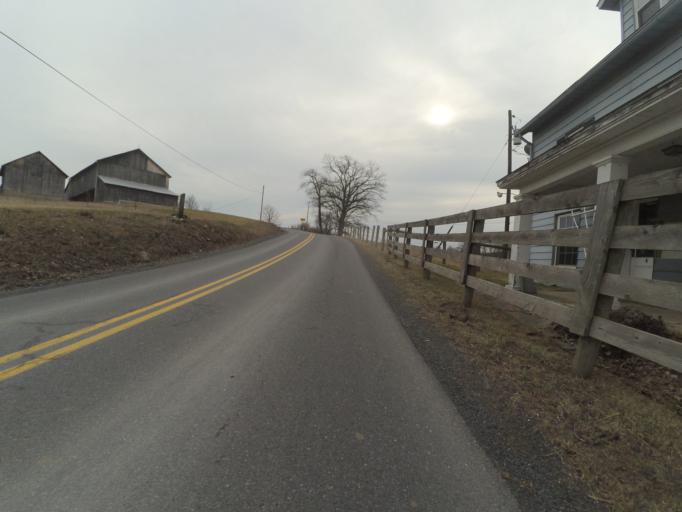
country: US
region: Pennsylvania
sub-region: Centre County
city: State College
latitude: 40.7666
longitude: -77.8413
